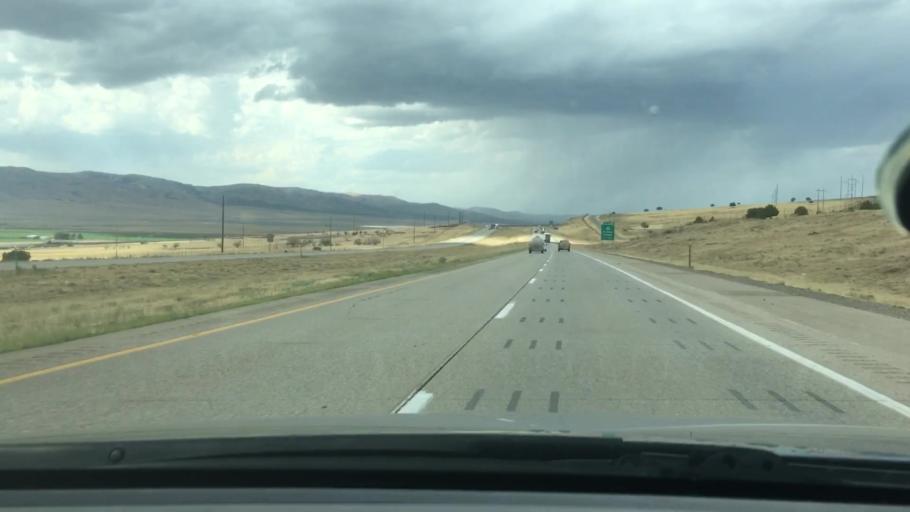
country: US
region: Utah
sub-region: Juab County
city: Nephi
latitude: 39.7370
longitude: -111.8266
